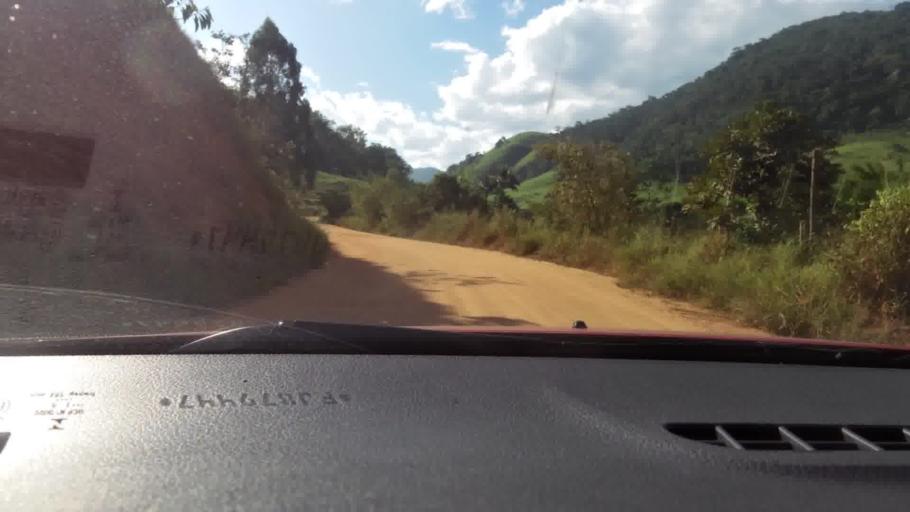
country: BR
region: Espirito Santo
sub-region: Guarapari
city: Guarapari
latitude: -20.5354
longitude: -40.5615
